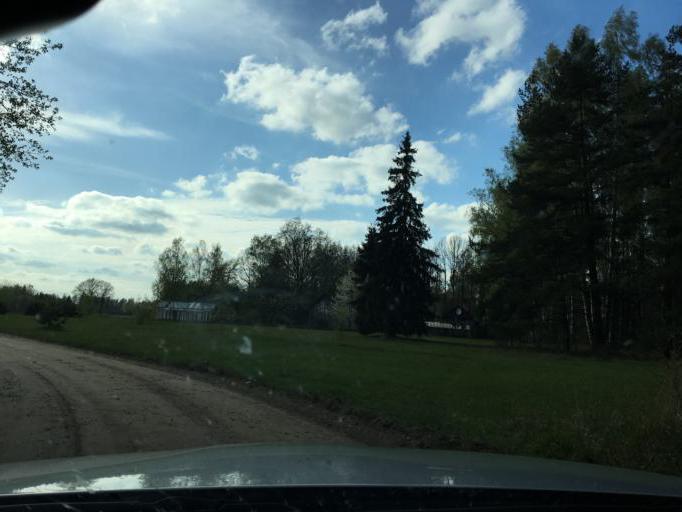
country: LV
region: Ozolnieku
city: Ozolnieki
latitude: 56.6723
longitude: 23.8720
